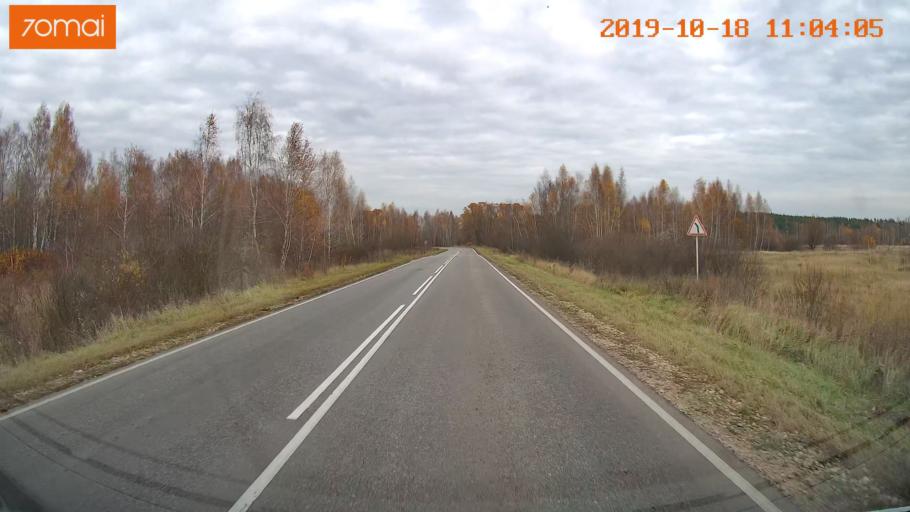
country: RU
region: Tula
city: Yepifan'
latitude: 53.8896
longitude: 38.5503
